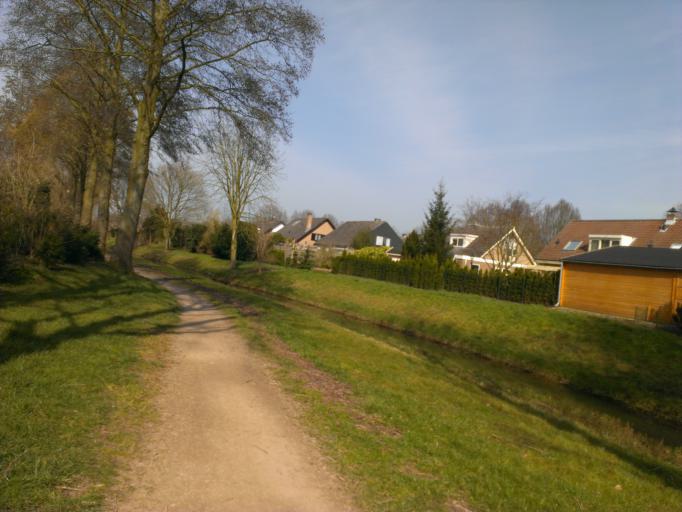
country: NL
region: Gelderland
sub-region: Gemeente Voorst
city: Twello
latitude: 52.2289
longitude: 6.1058
